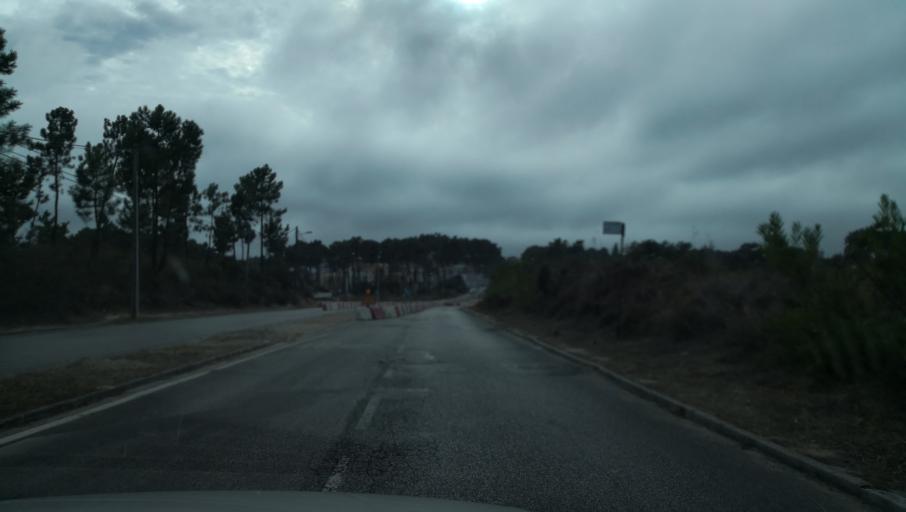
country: PT
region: Setubal
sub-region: Seixal
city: Amora
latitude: 38.5928
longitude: -9.1494
